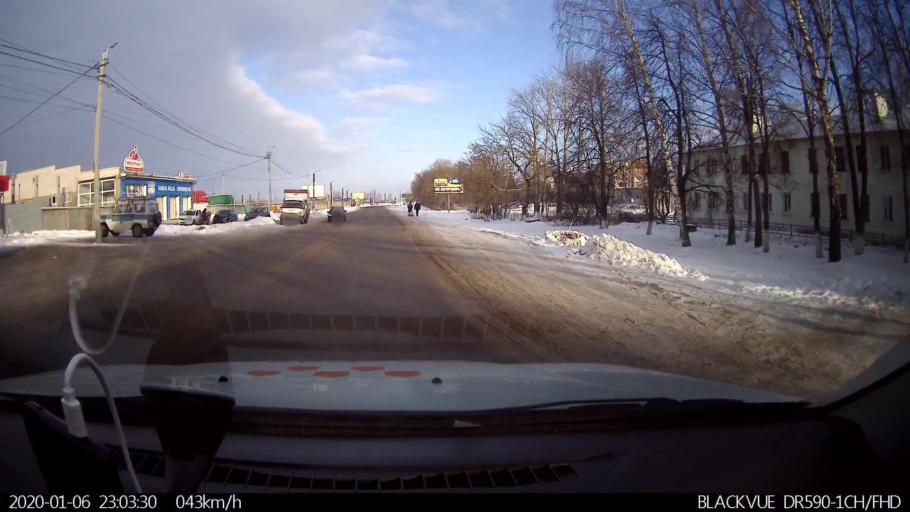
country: RU
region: Nizjnij Novgorod
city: Bogorodsk
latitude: 56.1130
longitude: 43.5345
